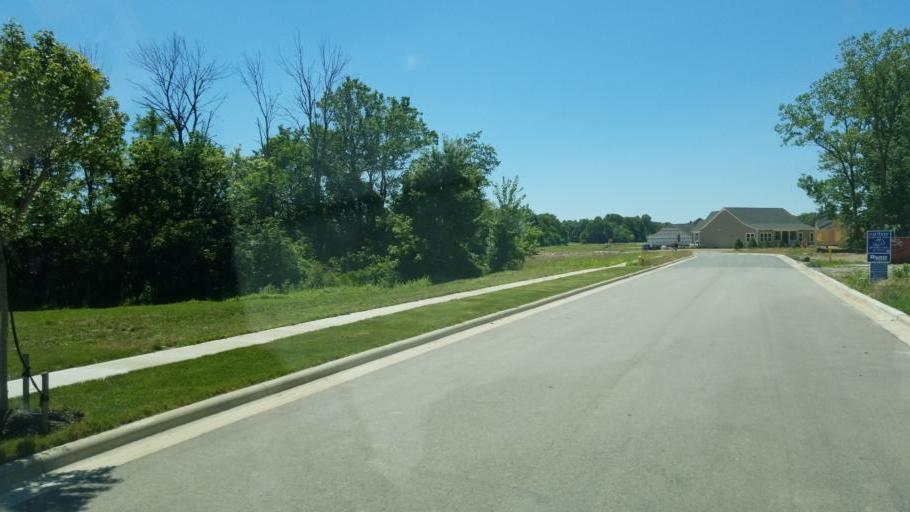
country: US
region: Ohio
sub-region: Delaware County
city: Sunbury
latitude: 40.1892
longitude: -82.9013
